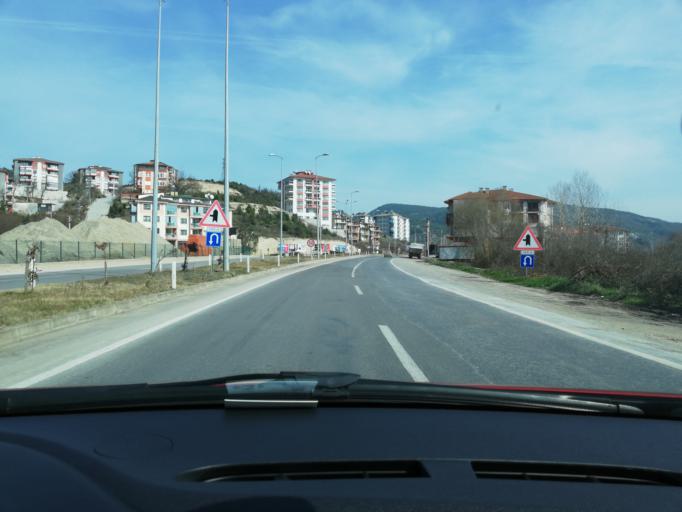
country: TR
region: Bartin
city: Bartin
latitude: 41.6418
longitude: 32.3557
